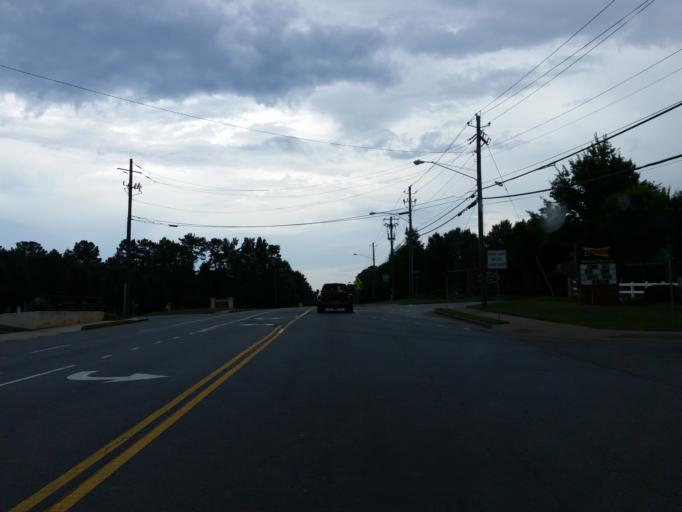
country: US
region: Georgia
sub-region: Fulton County
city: Roswell
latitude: 34.0488
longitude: -84.3611
